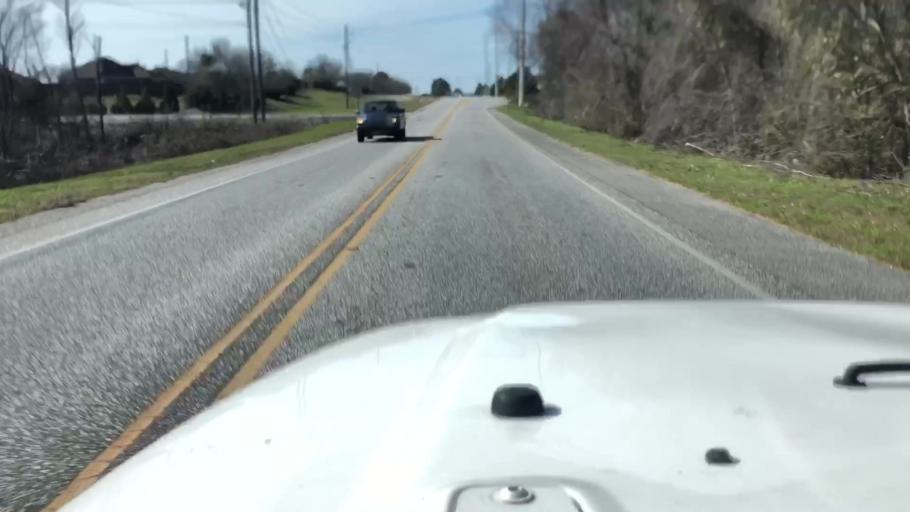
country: US
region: Alabama
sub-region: Elmore County
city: Blue Ridge
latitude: 32.3919
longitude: -86.1730
